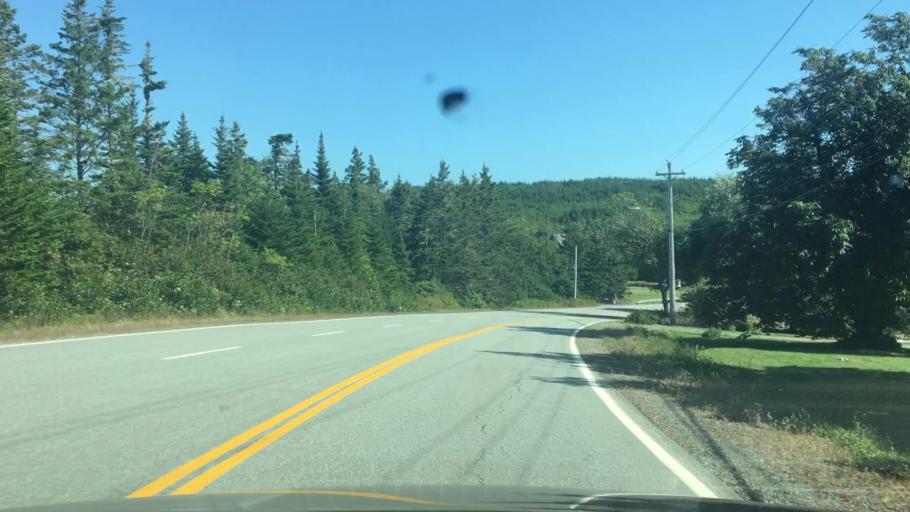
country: CA
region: Nova Scotia
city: New Glasgow
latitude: 44.8137
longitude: -62.6404
